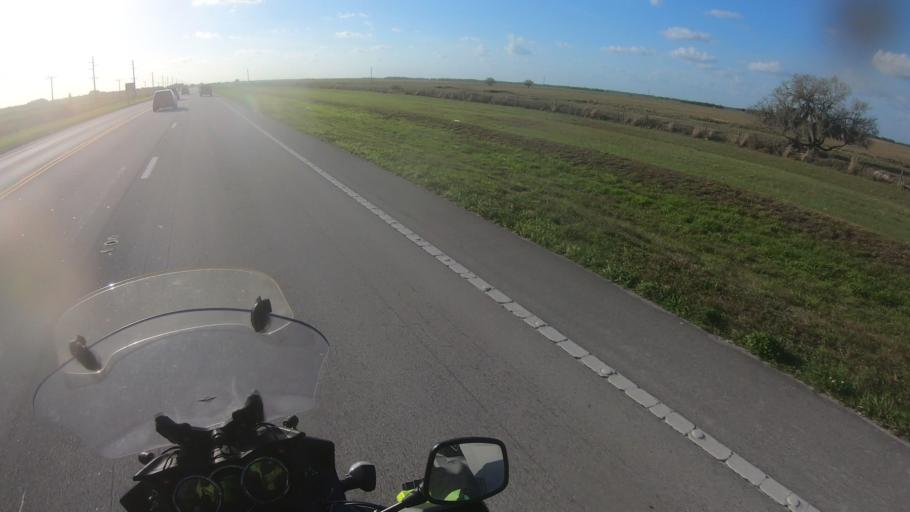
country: US
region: Florida
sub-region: DeSoto County
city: Southeast Arcadia
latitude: 27.2098
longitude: -81.7136
